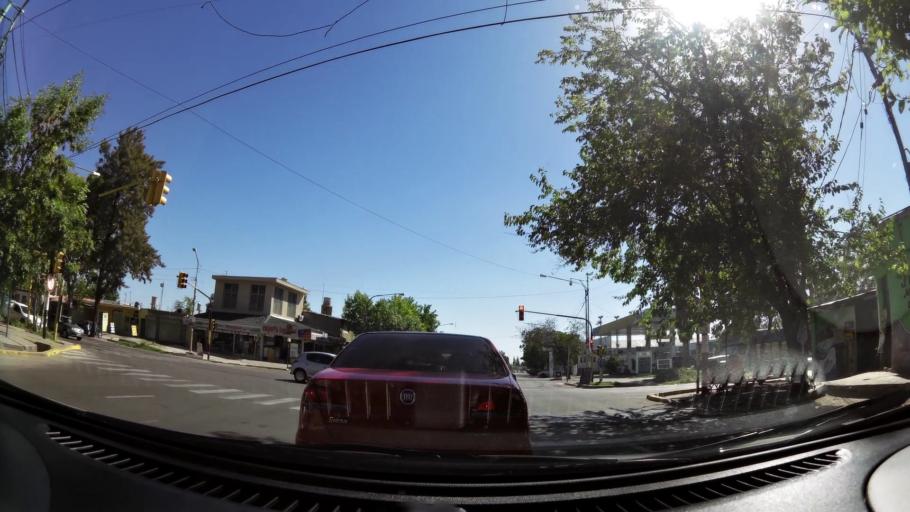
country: AR
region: Mendoza
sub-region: Departamento de Maipu
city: Maipu
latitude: -32.9504
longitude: -68.7875
